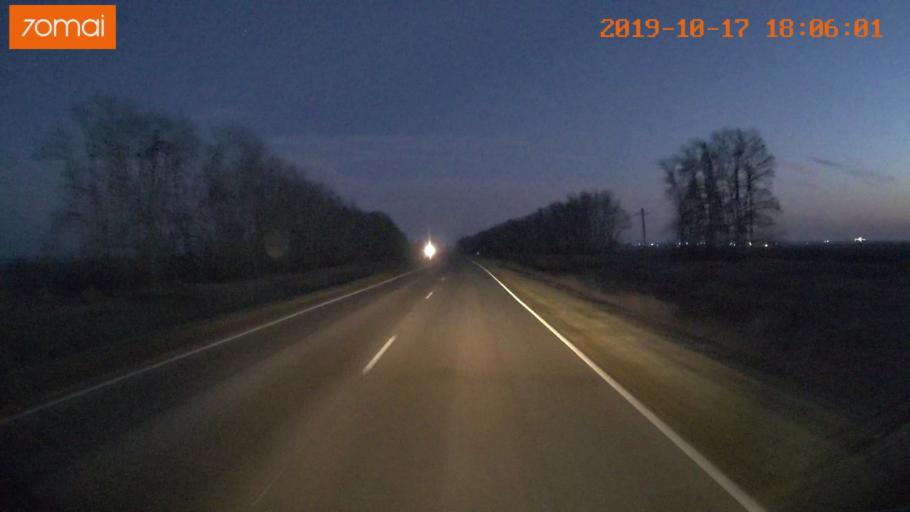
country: RU
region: Tula
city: Kurkino
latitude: 53.4576
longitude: 38.6507
